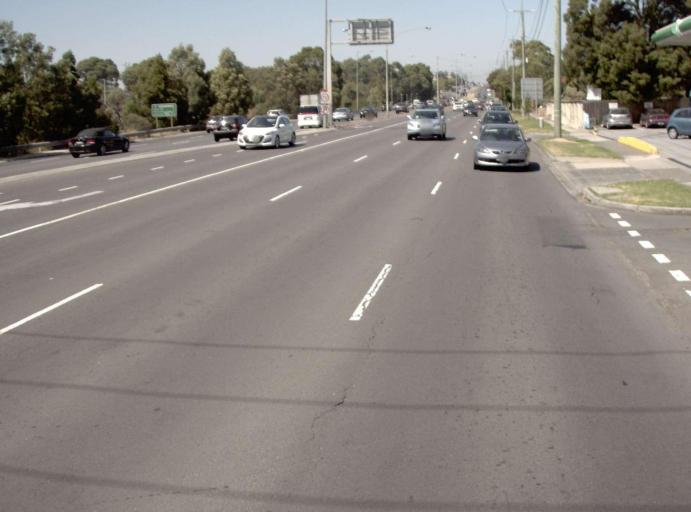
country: AU
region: Victoria
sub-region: Monash
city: Chadstone
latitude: -37.8842
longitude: 145.0898
